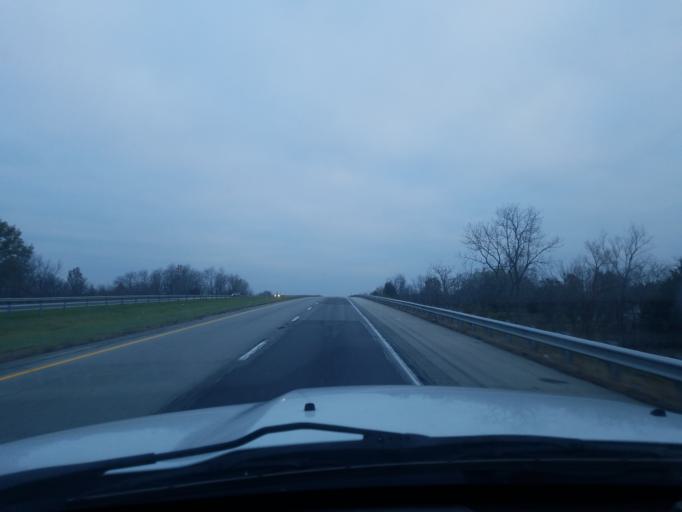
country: US
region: Indiana
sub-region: Madison County
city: Chesterfield
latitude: 40.0678
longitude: -85.5883
